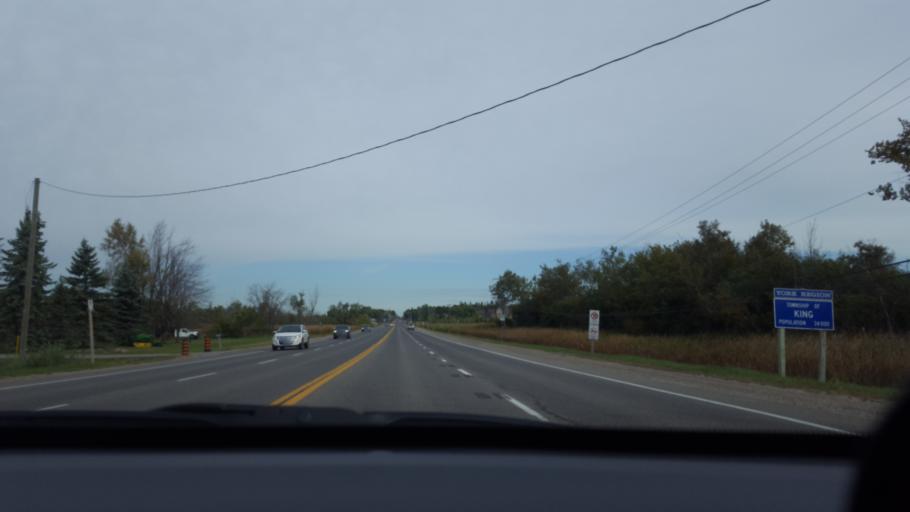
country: CA
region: Ontario
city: Vaughan
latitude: 43.9143
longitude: -79.5243
